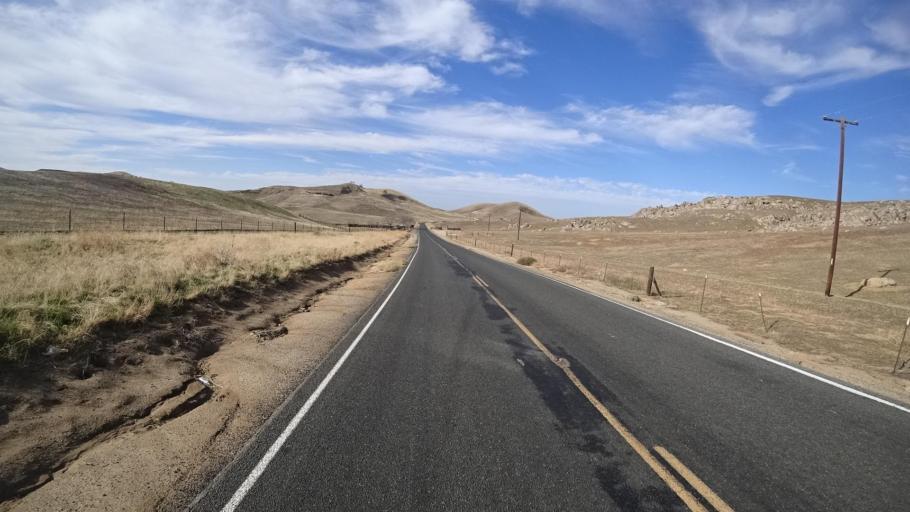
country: US
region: California
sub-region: Kern County
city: Oildale
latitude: 35.6130
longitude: -118.8697
